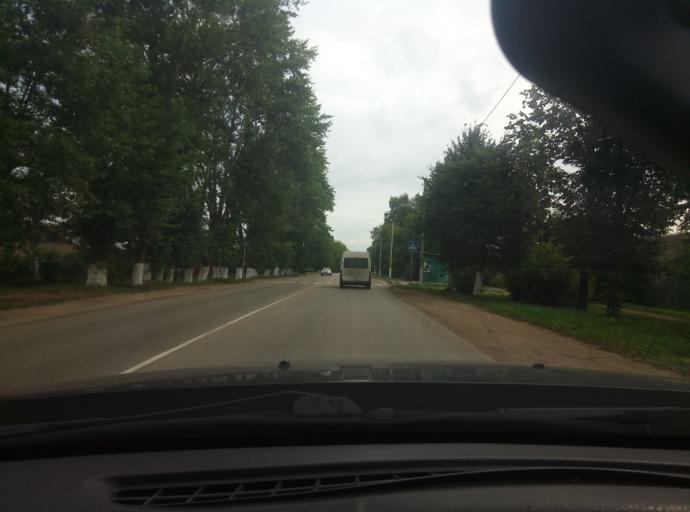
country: RU
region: Tula
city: Donskoy
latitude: 53.9685
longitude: 38.3499
